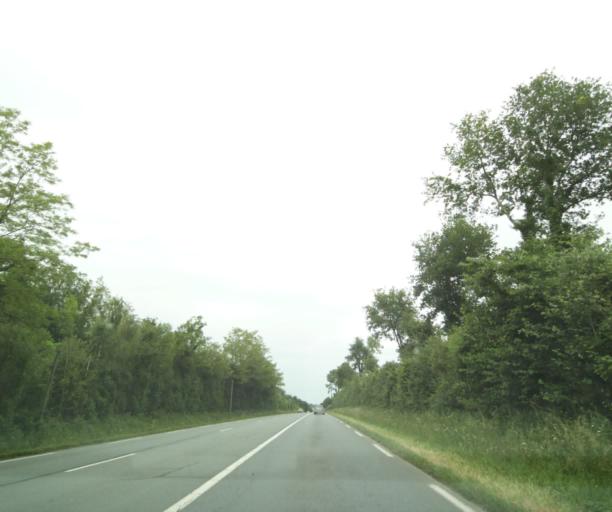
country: FR
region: Poitou-Charentes
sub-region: Departement des Deux-Sevres
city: Champdeniers-Saint-Denis
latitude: 46.5049
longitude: -0.3366
